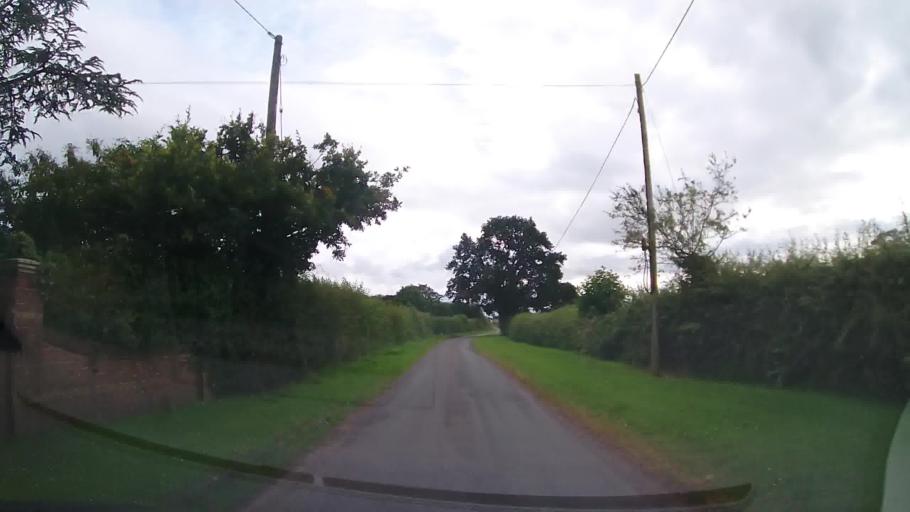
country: GB
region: England
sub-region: Shropshire
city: Prees
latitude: 52.9164
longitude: -2.6970
